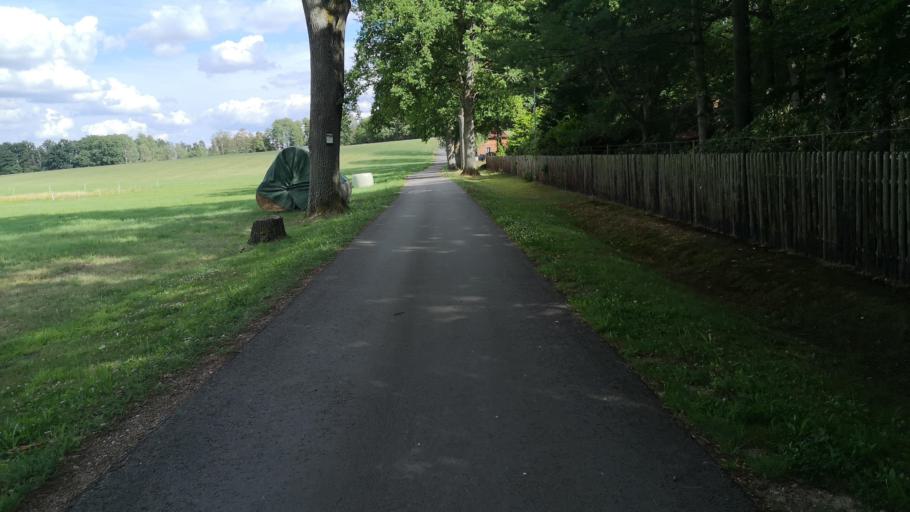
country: DE
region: Lower Saxony
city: Thomasburg
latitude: 53.2205
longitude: 10.6730
